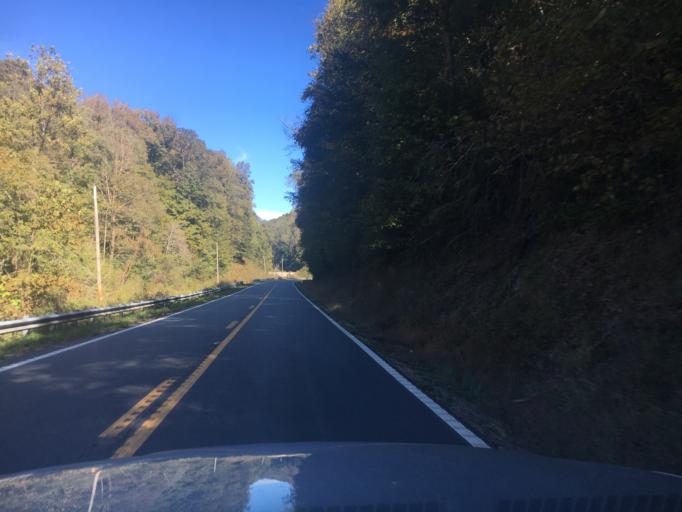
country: US
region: North Carolina
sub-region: Burke County
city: Glen Alpine
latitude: 35.5661
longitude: -81.8511
